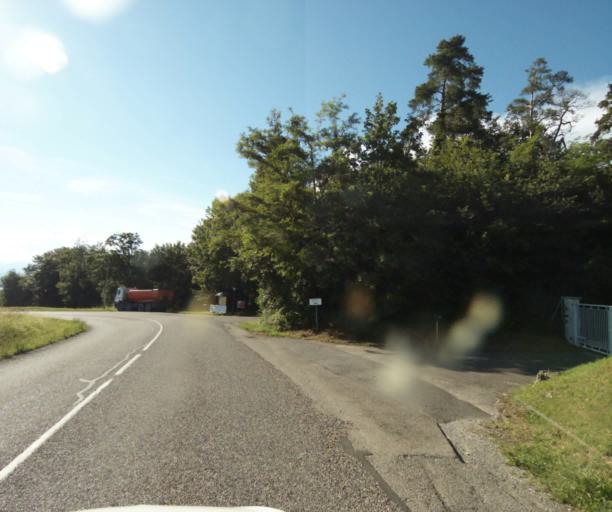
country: FR
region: Rhone-Alpes
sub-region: Departement de la Haute-Savoie
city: Ballaison
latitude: 46.3010
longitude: 6.3256
